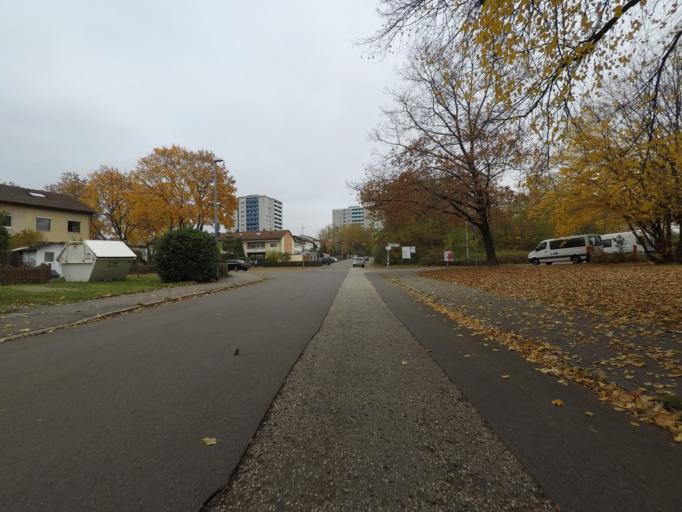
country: DE
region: Baden-Wuerttemberg
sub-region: Tuebingen Region
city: Reutlingen
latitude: 48.5118
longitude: 9.2105
